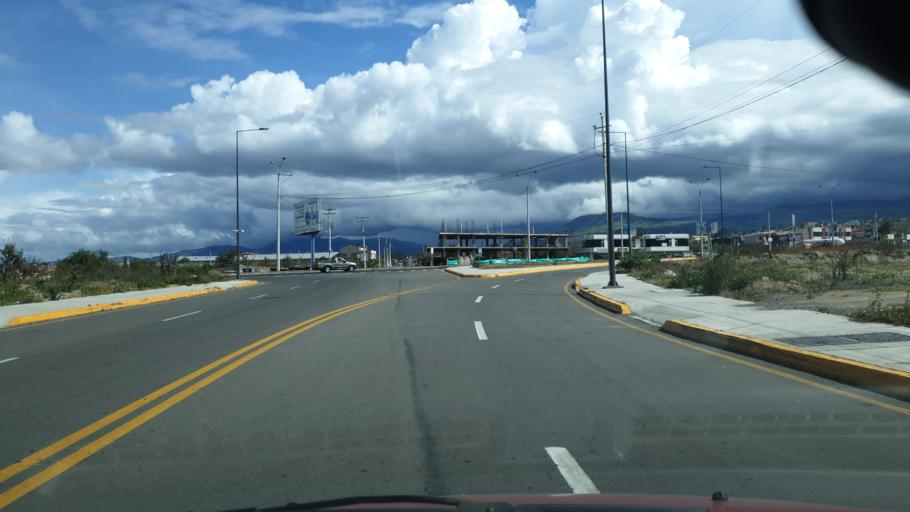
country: EC
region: Tungurahua
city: Ambato
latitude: -1.2998
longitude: -78.6319
